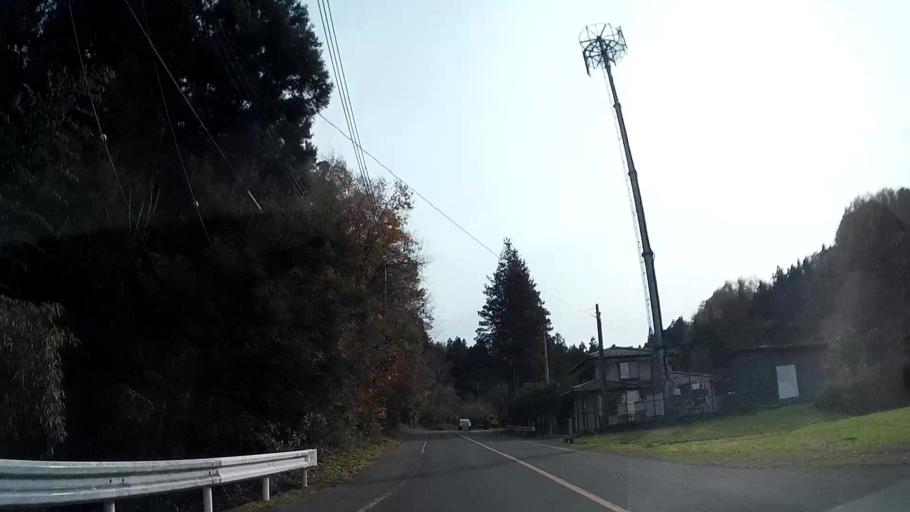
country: JP
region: Saitama
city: Chichibu
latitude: 35.9825
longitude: 139.0381
